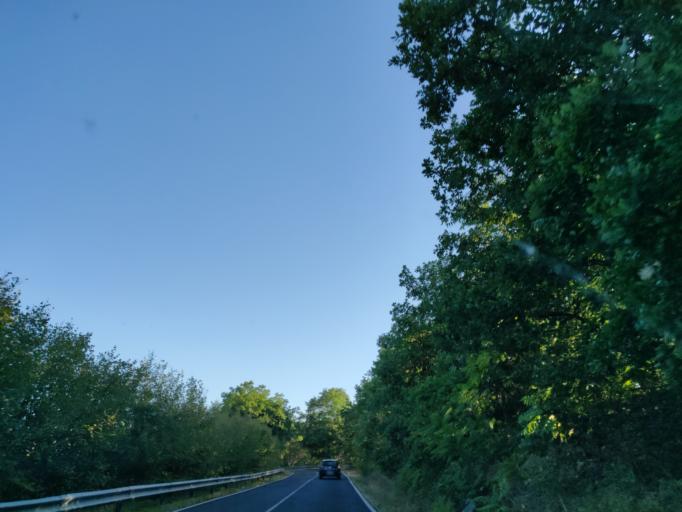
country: IT
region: Latium
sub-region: Provincia di Viterbo
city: Gradoli
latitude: 42.6475
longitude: 11.8407
